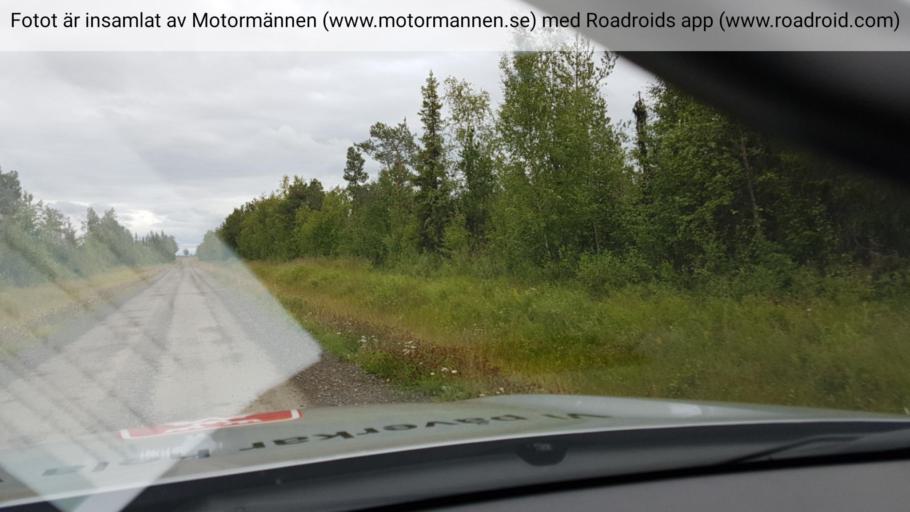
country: SE
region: Norrbotten
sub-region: Pajala Kommun
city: Pajala
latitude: 67.0829
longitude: 22.7727
